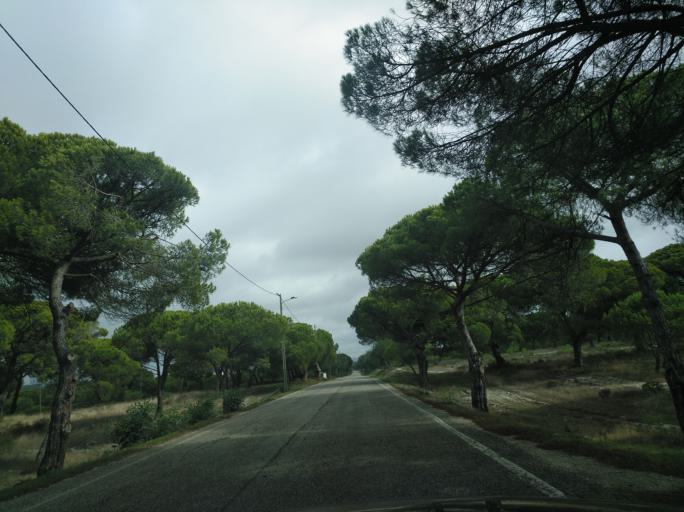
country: PT
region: Setubal
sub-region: Santiago do Cacem
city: Santo Andre
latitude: 38.1324
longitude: -8.7727
